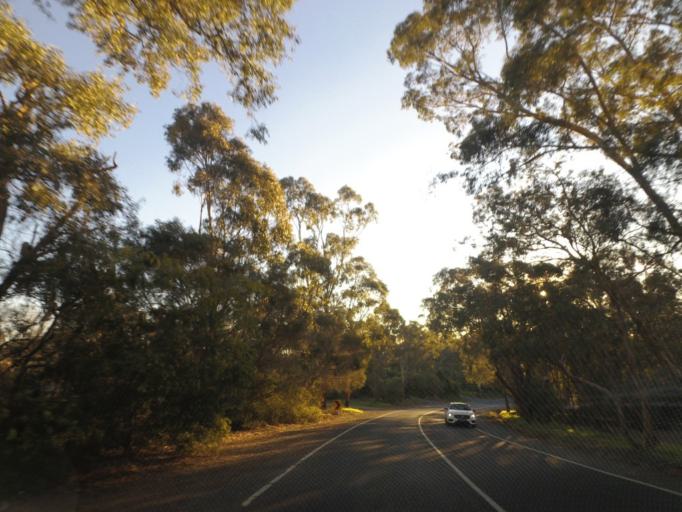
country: AU
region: Victoria
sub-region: Manningham
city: Park Orchards
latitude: -37.7598
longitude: 145.2120
